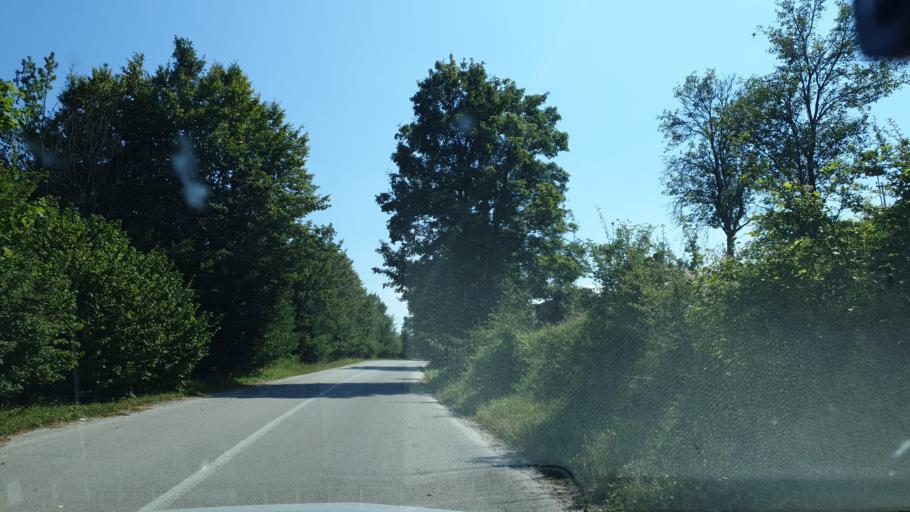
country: RS
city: Zlatibor
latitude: 43.6579
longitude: 19.8322
